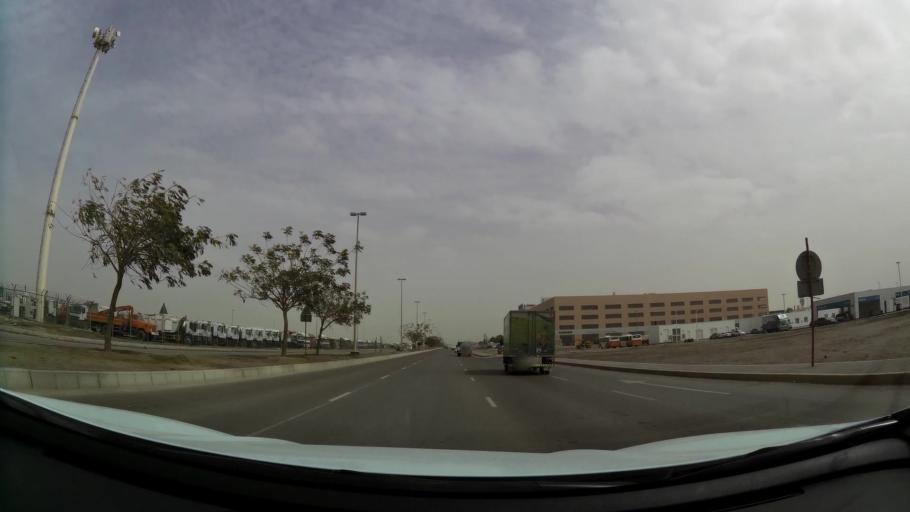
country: AE
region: Abu Dhabi
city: Abu Dhabi
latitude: 24.3581
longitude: 54.4736
